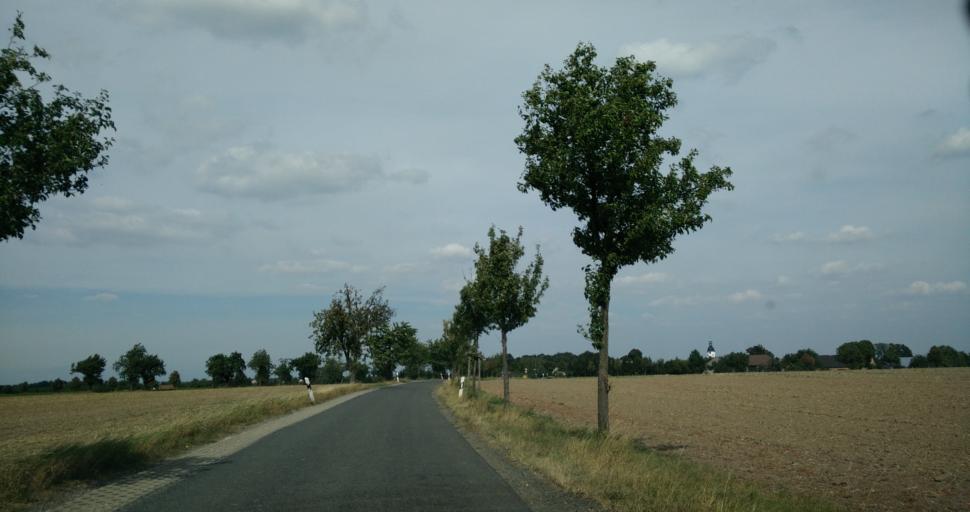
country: DE
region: Saxony
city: Bad Lausick
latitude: 51.1322
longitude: 12.6895
